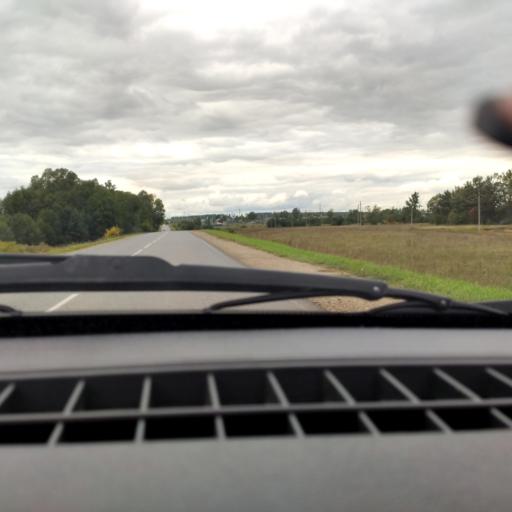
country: RU
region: Bashkortostan
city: Iglino
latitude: 54.7281
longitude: 56.4044
